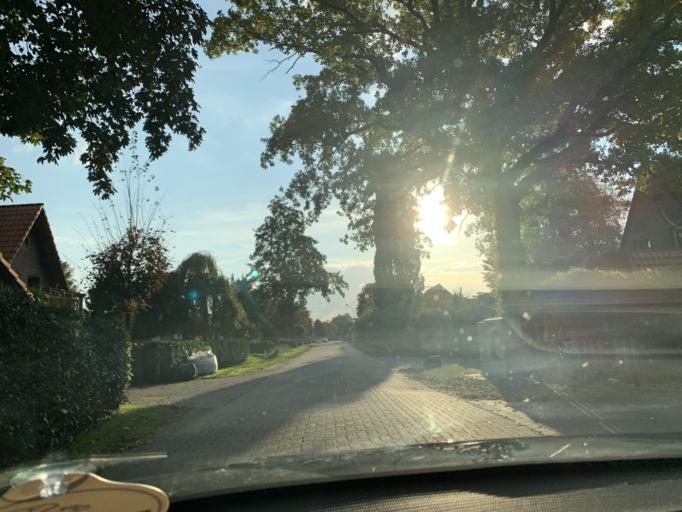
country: DE
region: Lower Saxony
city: Apen
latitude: 53.2360
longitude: 7.7784
